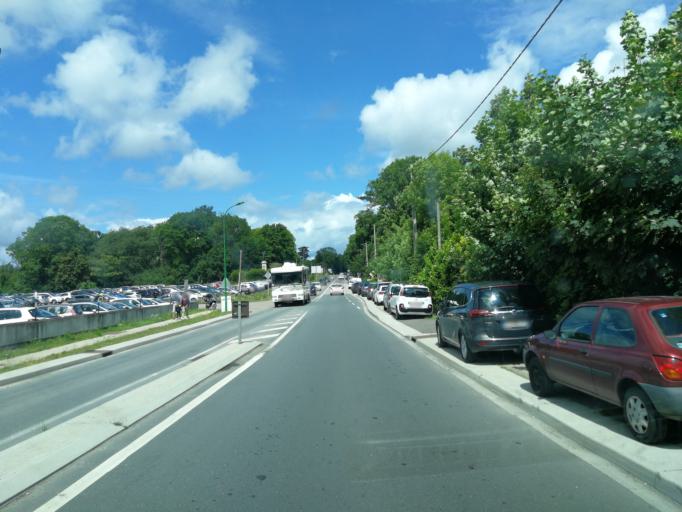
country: FR
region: Haute-Normandie
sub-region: Departement de la Seine-Maritime
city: Sahurs
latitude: 49.3451
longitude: 0.9320
